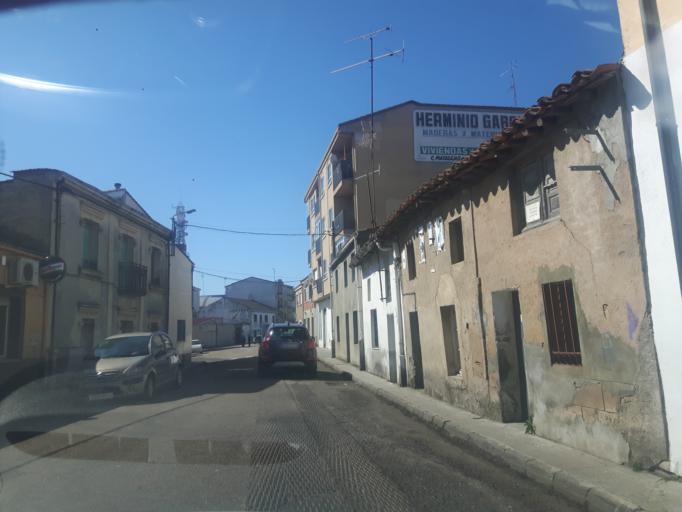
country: ES
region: Castille and Leon
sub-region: Provincia de Salamanca
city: Vitigudino
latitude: 41.0118
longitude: -6.4344
